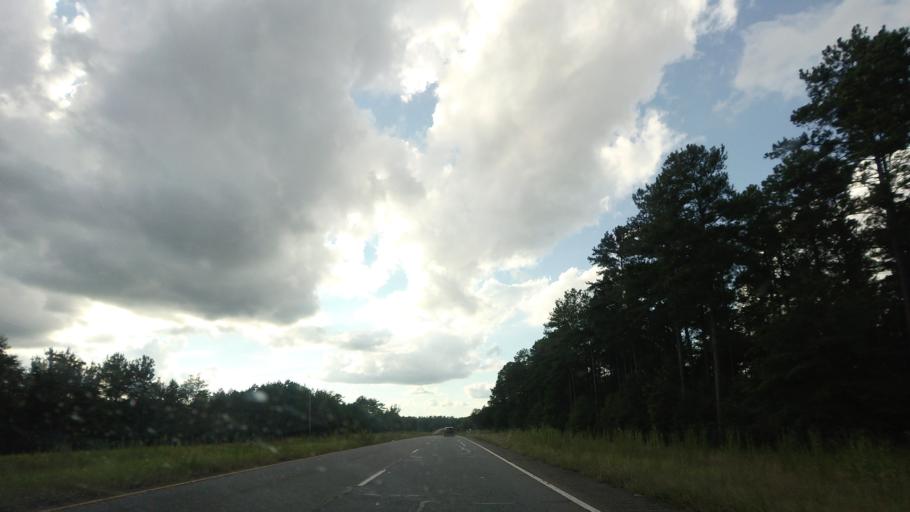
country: US
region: Georgia
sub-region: Houston County
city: Perry
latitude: 32.4155
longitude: -83.6886
